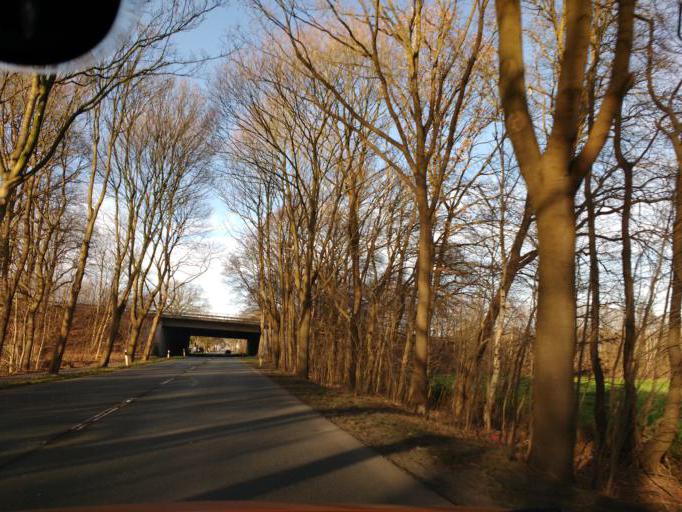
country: DE
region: Lower Saxony
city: Oldenburg
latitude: 53.1084
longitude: 8.2735
